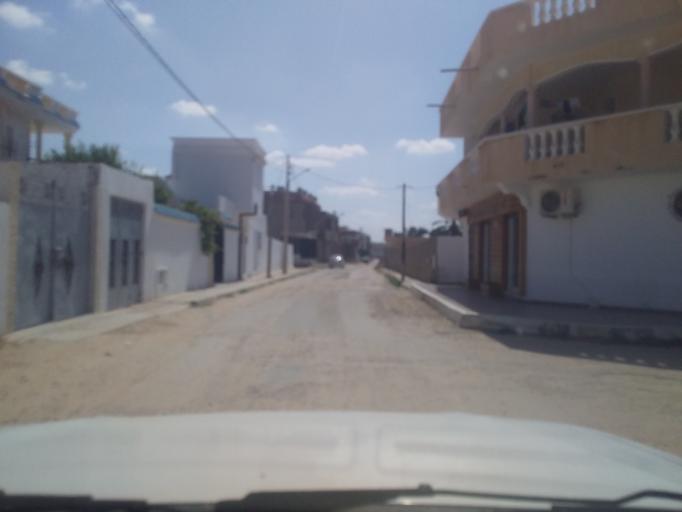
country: TN
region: Qabis
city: Matmata
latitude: 33.6163
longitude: 10.2920
